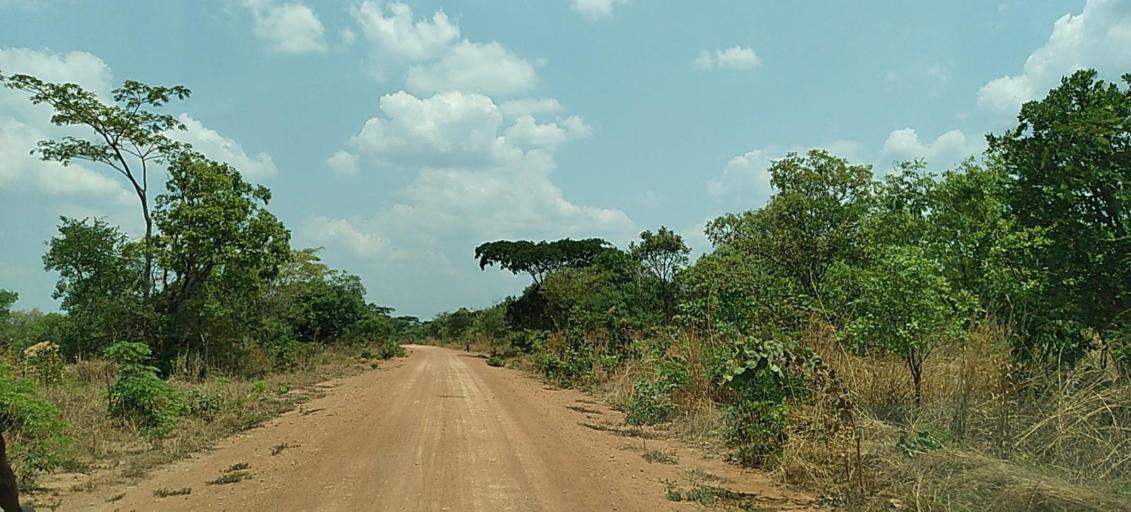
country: ZM
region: Copperbelt
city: Luanshya
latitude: -13.1402
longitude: 28.3148
